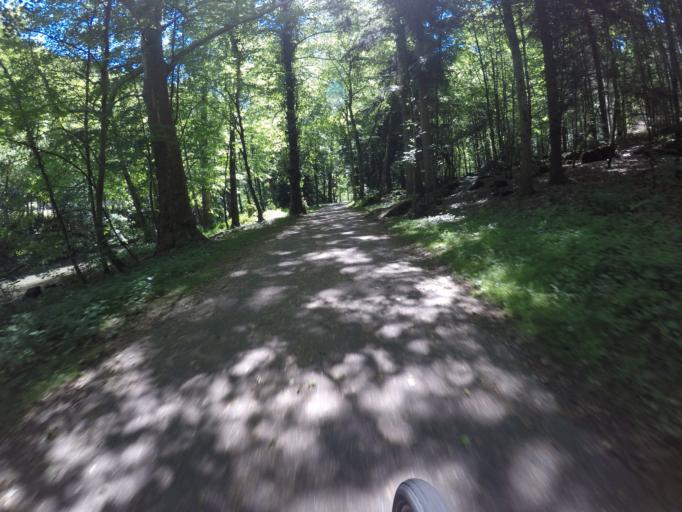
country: DE
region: Baden-Wuerttemberg
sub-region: Karlsruhe Region
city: Pforzheim
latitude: 48.8698
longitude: 8.7123
